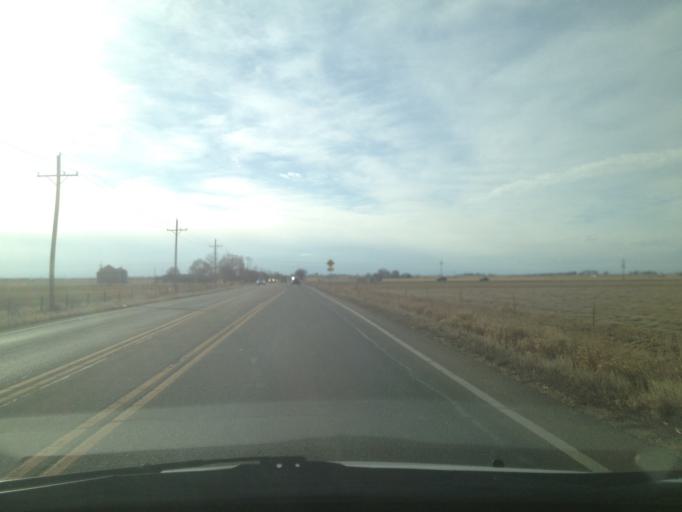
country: US
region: Colorado
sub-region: Weld County
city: Hudson
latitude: 40.0807
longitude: -104.6747
